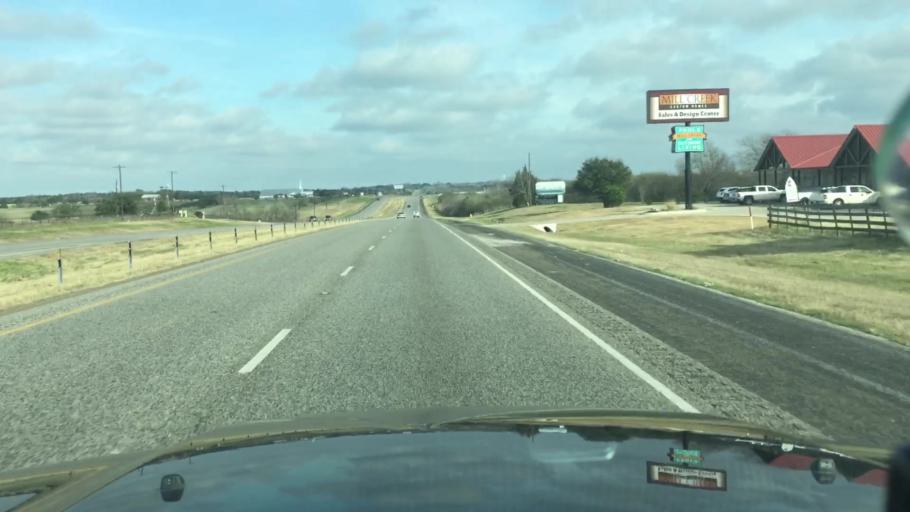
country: US
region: Texas
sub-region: Washington County
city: Brenham
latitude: 30.1407
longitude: -96.2924
